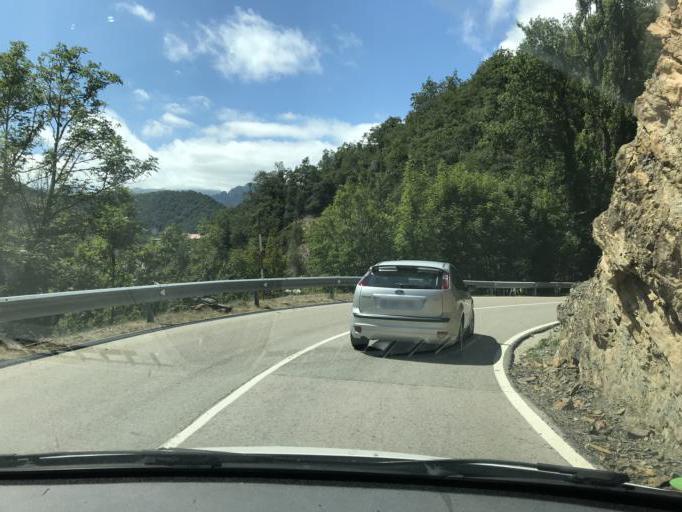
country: ES
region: Cantabria
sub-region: Provincia de Cantabria
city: Cabezon de Liebana
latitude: 43.0770
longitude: -4.4899
